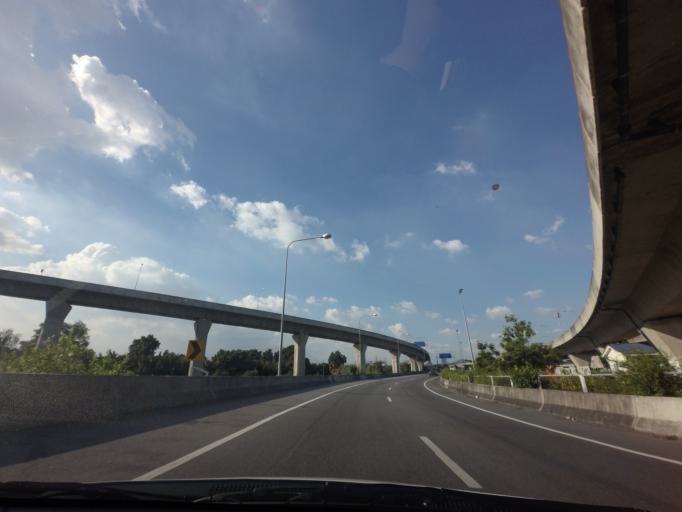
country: TH
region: Samut Prakan
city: Phra Pradaeng
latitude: 13.6388
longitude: 100.5502
